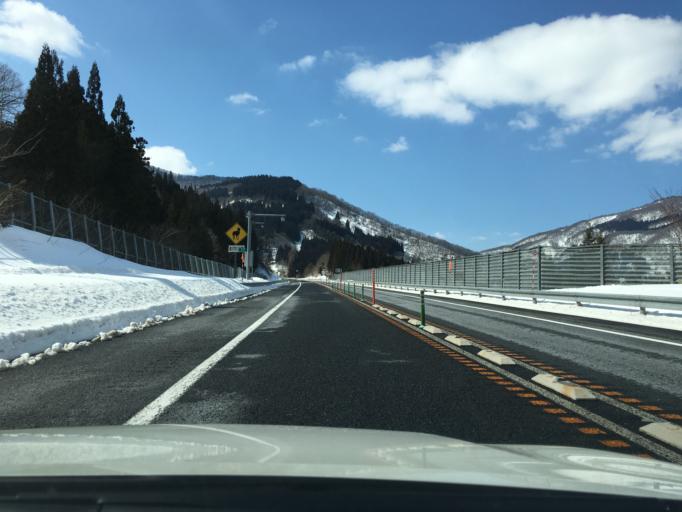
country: JP
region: Yamagata
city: Sagae
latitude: 38.4440
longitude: 140.0571
